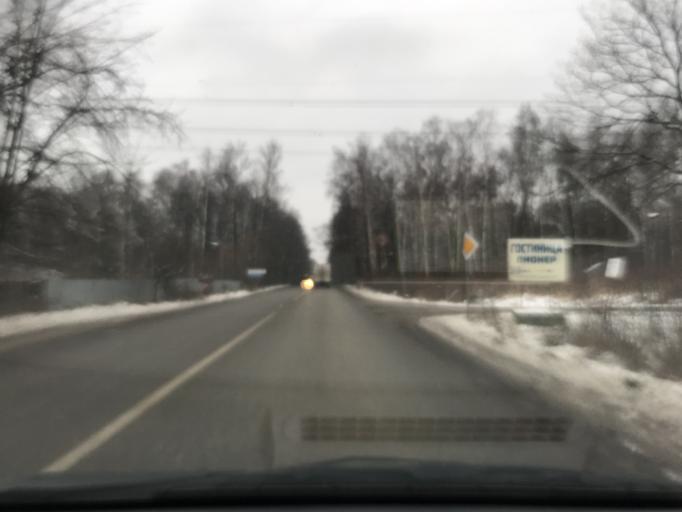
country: RU
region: Moskovskaya
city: Elektrostal'
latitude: 55.8209
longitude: 38.4546
